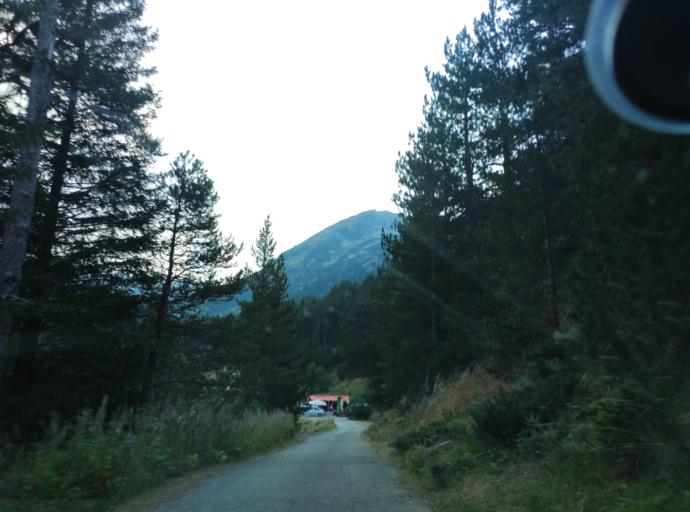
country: BG
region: Blagoevgrad
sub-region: Obshtina Bansko
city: Bansko
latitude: 41.7673
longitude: 23.4254
